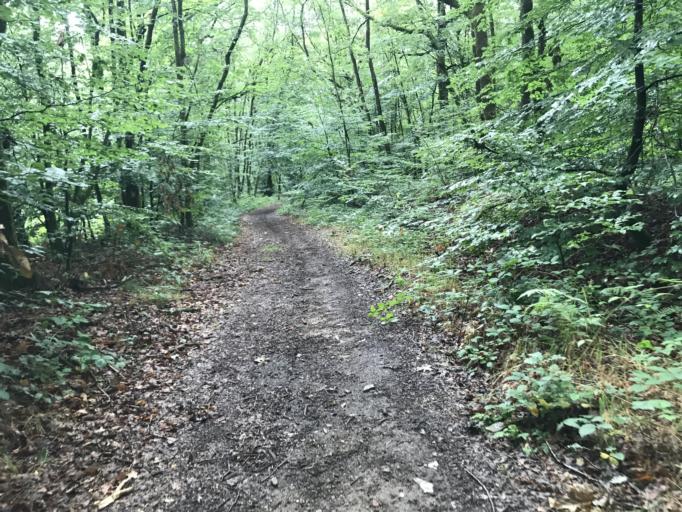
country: FR
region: Champagne-Ardenne
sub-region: Departement des Ardennes
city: Thilay
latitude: 49.8938
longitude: 4.7823
